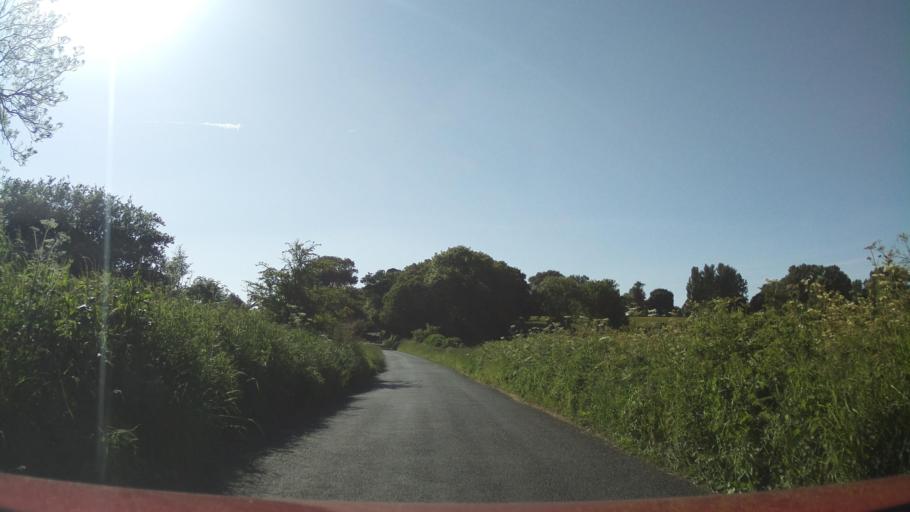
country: GB
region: England
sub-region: Somerset
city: Yeovil
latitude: 50.9353
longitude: -2.5960
